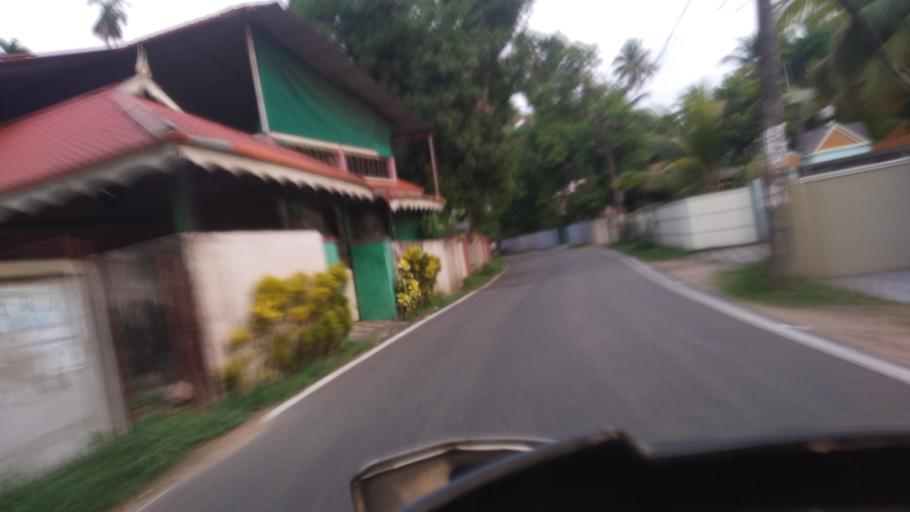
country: IN
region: Kerala
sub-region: Thrissur District
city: Kodungallur
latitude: 10.1606
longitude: 76.2105
